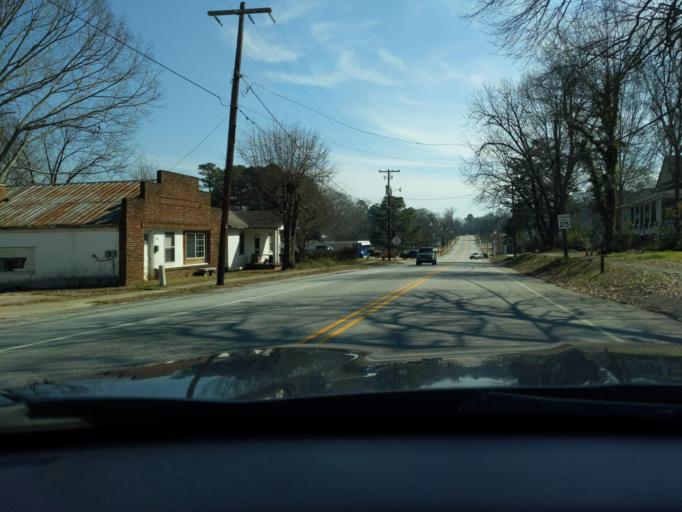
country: US
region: South Carolina
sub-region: Abbeville County
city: Calhoun Falls
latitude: 34.0918
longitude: -82.5951
